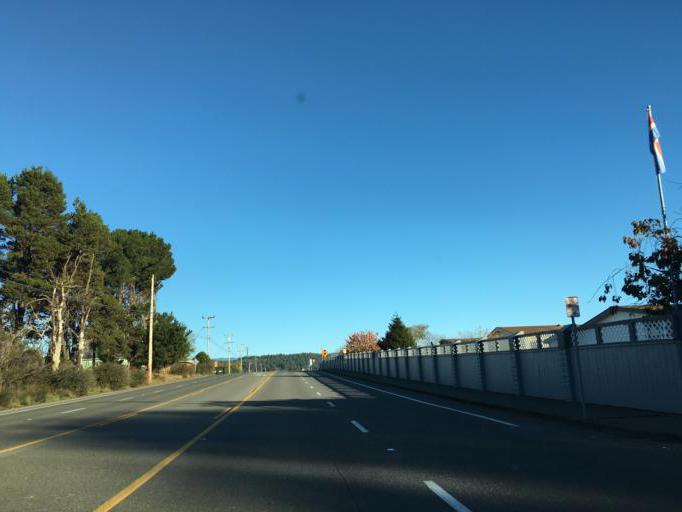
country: US
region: California
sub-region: Humboldt County
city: McKinleyville
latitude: 40.9562
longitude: -124.1134
